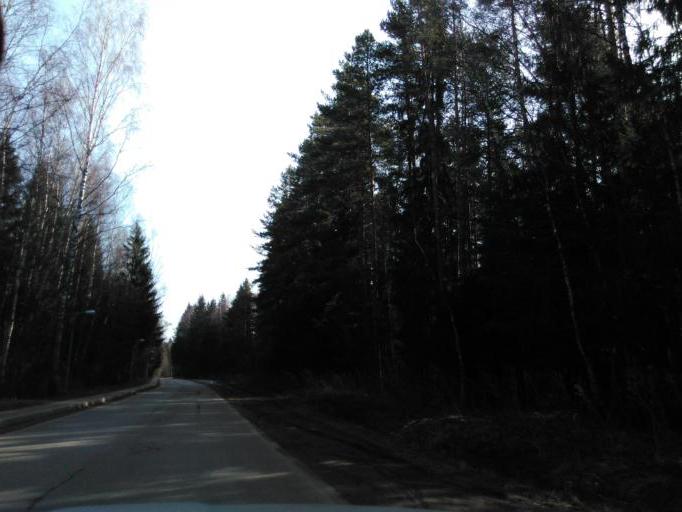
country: RU
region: Moskovskaya
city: Firsanovka
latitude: 55.9158
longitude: 37.2002
